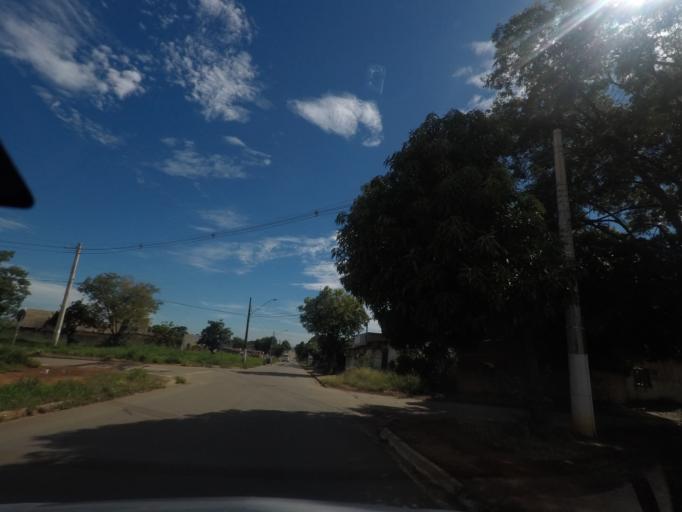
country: BR
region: Goias
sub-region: Aparecida De Goiania
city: Aparecida de Goiania
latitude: -16.8175
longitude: -49.2928
